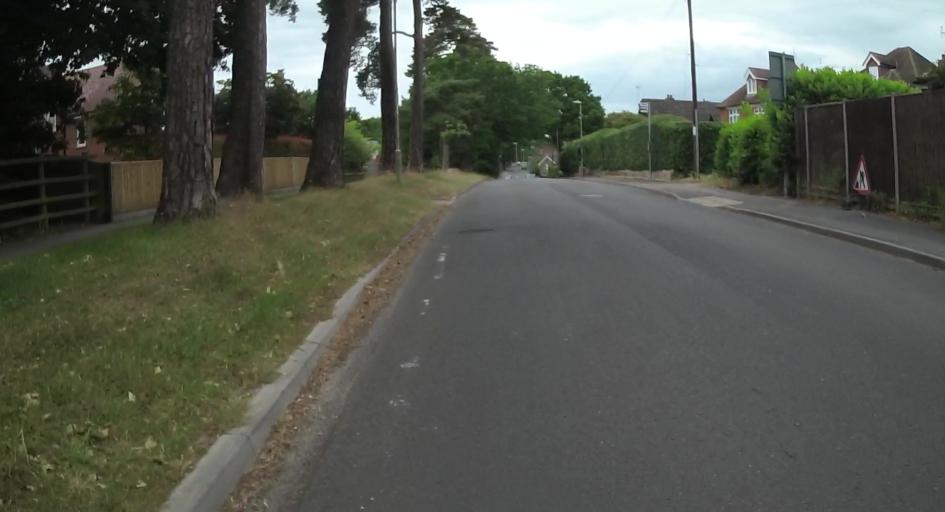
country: GB
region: England
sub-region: Hampshire
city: Fleet
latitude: 51.2589
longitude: -0.8348
